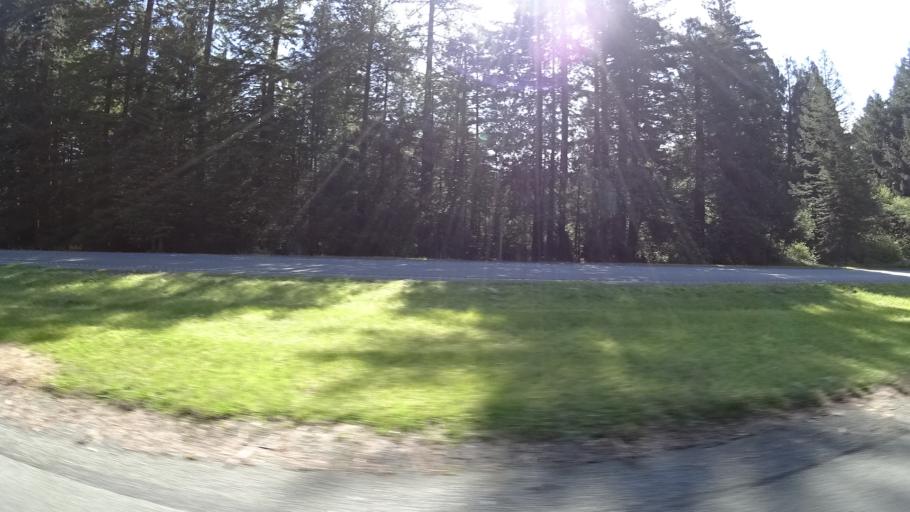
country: US
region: California
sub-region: Del Norte County
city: Bertsch-Oceanview
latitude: 41.8100
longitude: -124.1473
